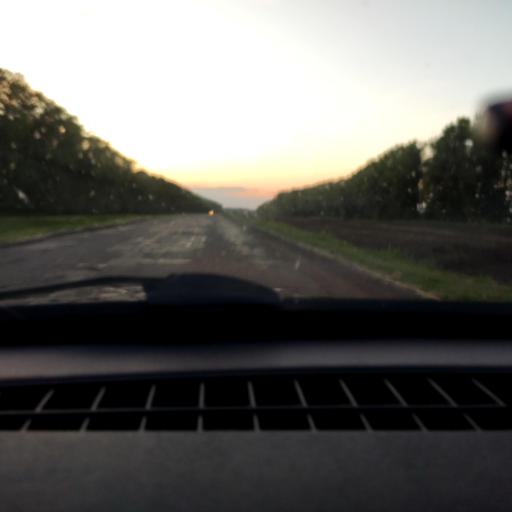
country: RU
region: Bashkortostan
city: Karmaskaly
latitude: 54.3884
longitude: 56.1761
